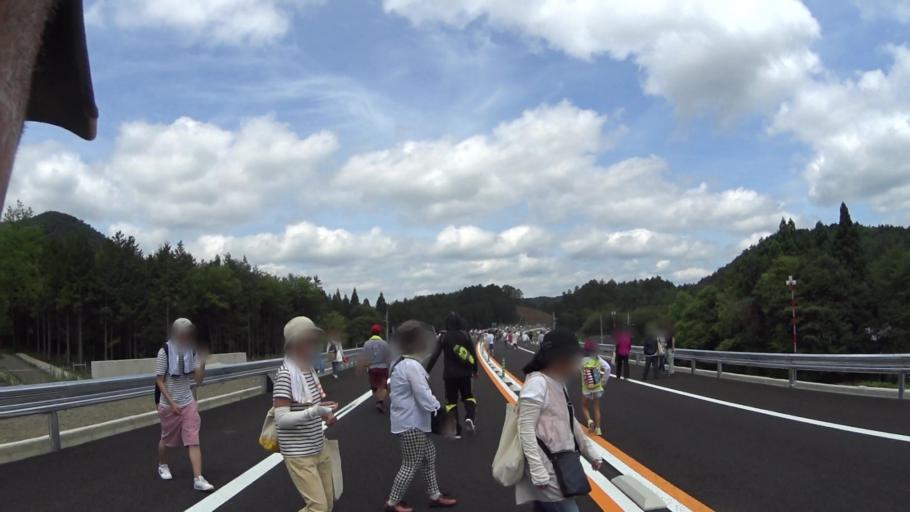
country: JP
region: Kyoto
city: Ayabe
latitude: 35.1607
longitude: 135.3930
